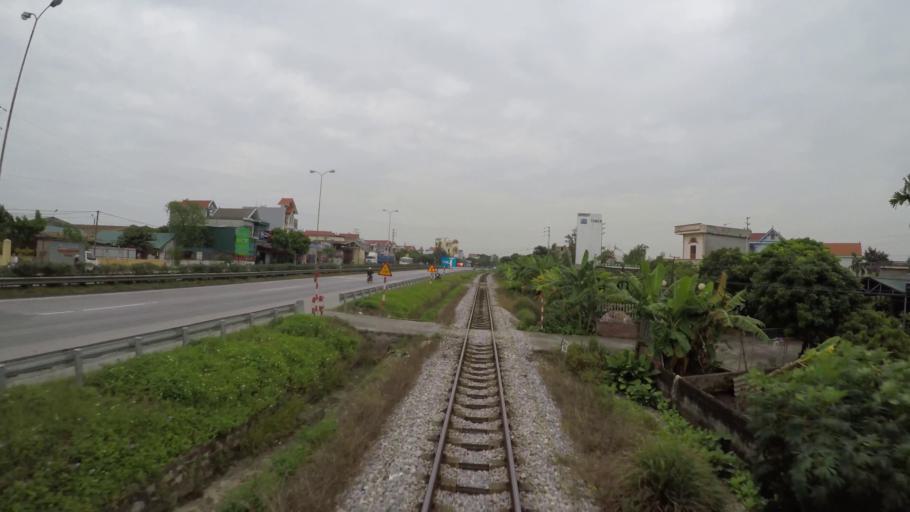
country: VN
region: Hai Duong
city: Phu Thai
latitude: 20.9684
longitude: 106.4565
